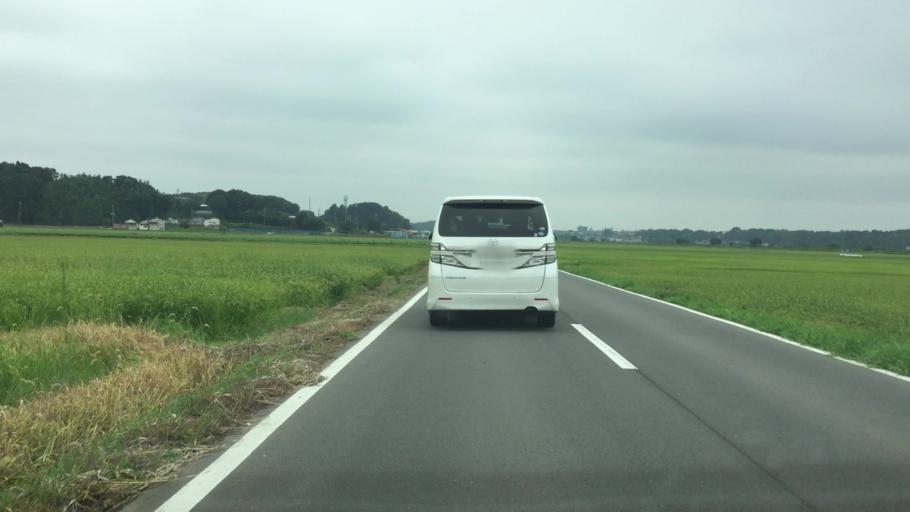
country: JP
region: Chiba
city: Abiko
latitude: 35.8442
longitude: 140.0508
